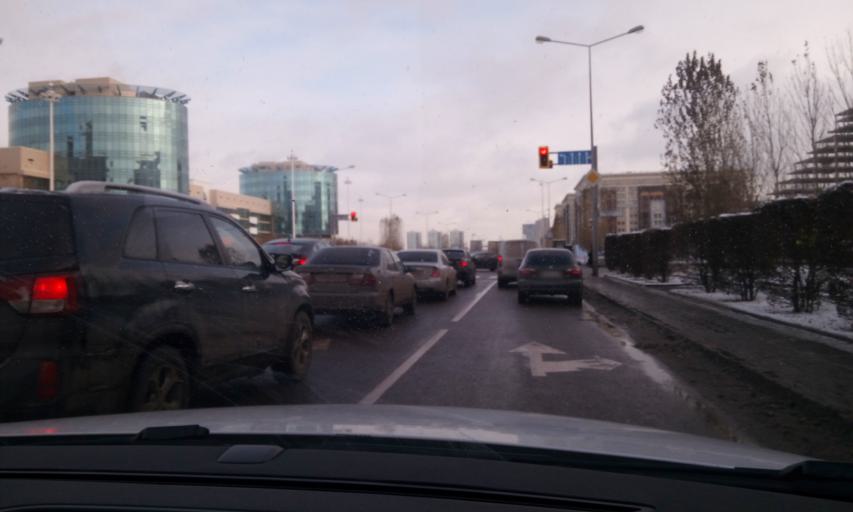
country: KZ
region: Astana Qalasy
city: Astana
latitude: 51.1340
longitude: 71.4300
